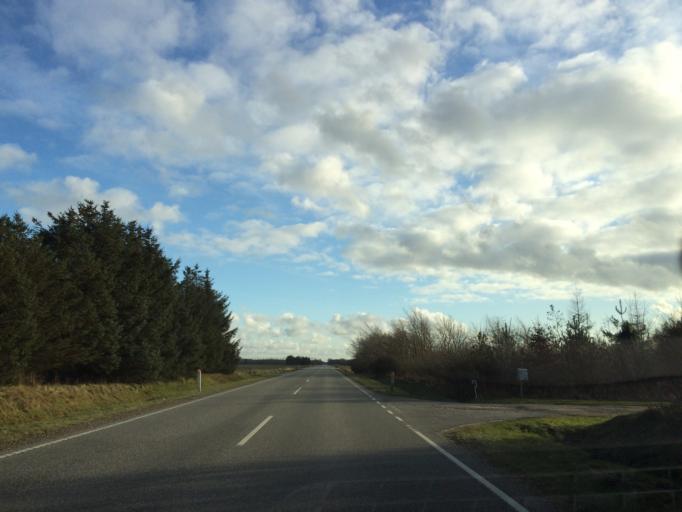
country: DK
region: Central Jutland
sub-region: Holstebro Kommune
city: Ulfborg
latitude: 56.3945
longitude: 8.3202
